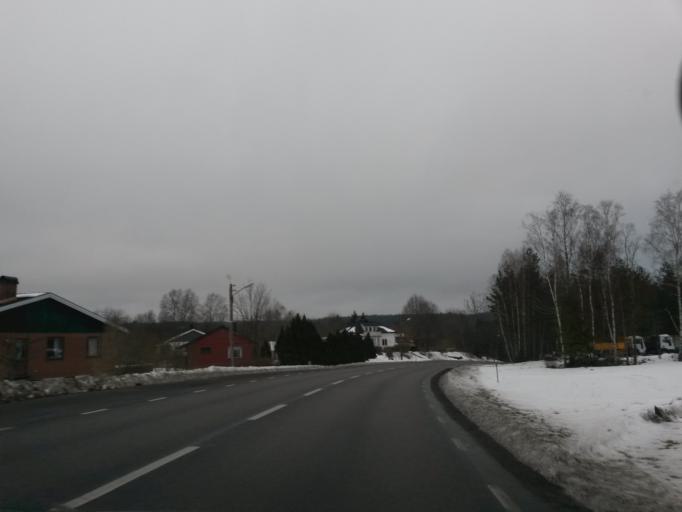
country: SE
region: Vaestra Goetaland
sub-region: Boras Kommun
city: Sandared
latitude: 57.8087
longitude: 12.7521
